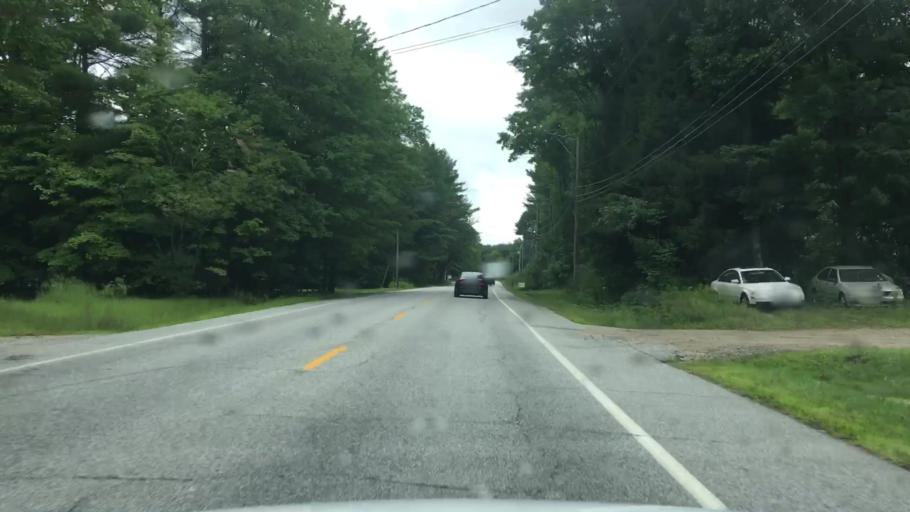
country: US
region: Maine
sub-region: York County
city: Cornish
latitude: 43.8246
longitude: -70.7742
